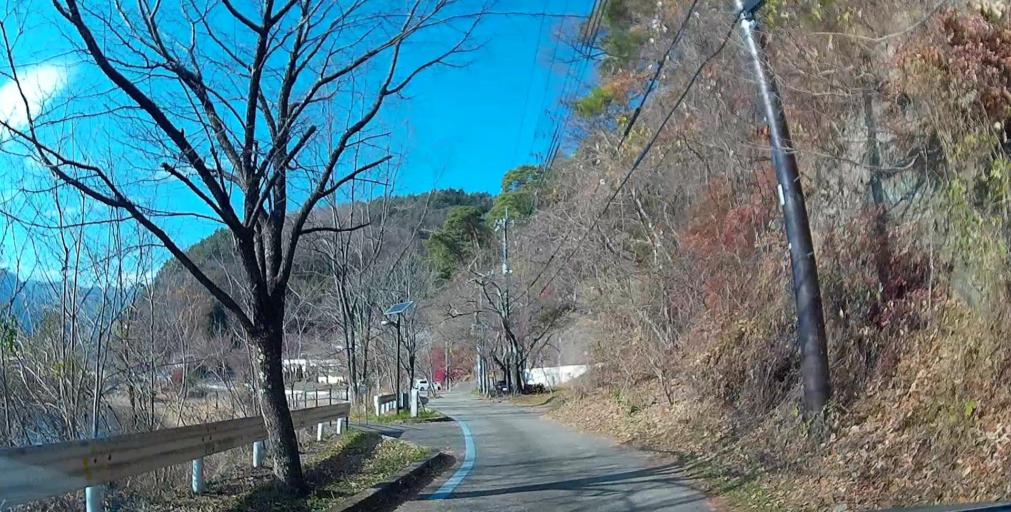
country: JP
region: Yamanashi
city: Fujikawaguchiko
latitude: 35.5222
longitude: 138.7558
